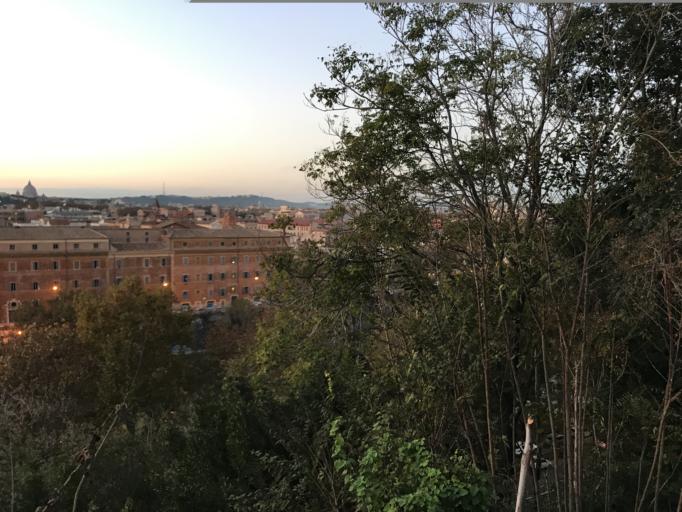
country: VA
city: Vatican City
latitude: 41.8844
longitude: 12.4784
